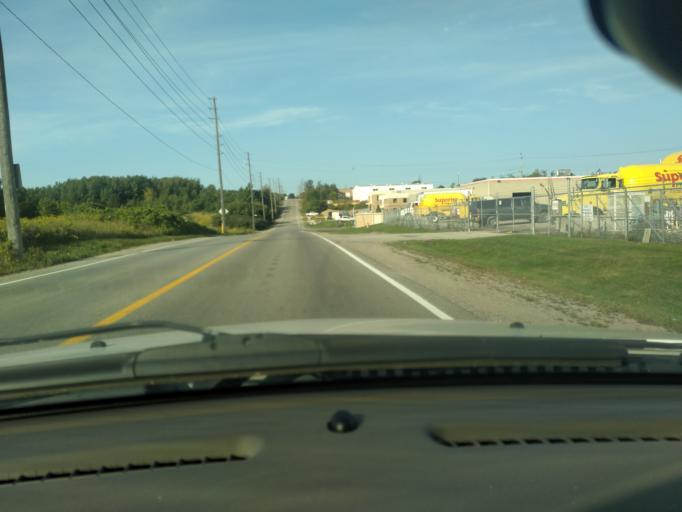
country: CA
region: Ontario
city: Innisfil
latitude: 44.3253
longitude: -79.6741
